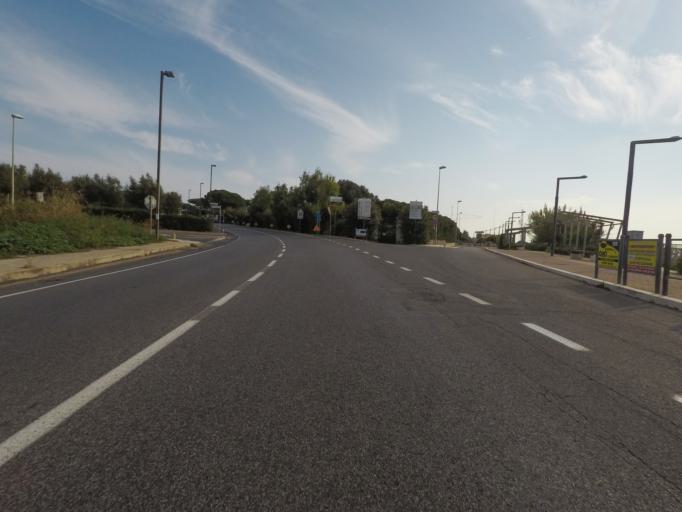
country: IT
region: Latium
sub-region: Citta metropolitana di Roma Capitale
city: Santa Marinella
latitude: 42.0358
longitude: 11.8333
